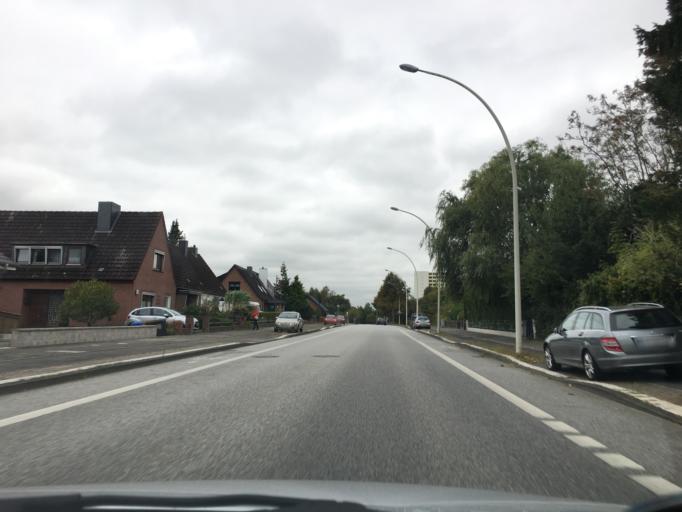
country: DE
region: Schleswig-Holstein
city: Melsdorf
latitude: 54.3171
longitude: 10.0598
